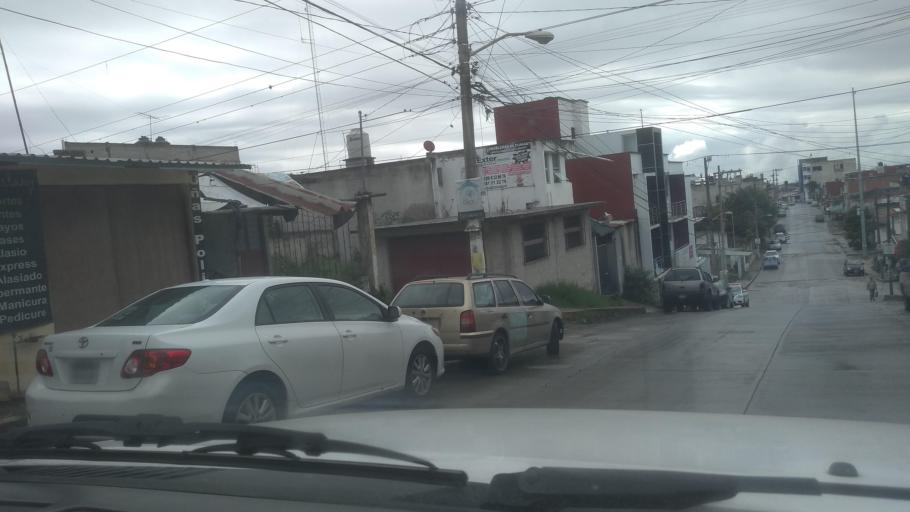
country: MX
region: Veracruz
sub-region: Xalapa
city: Colonia Santa Barbara
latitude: 19.5066
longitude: -96.8754
